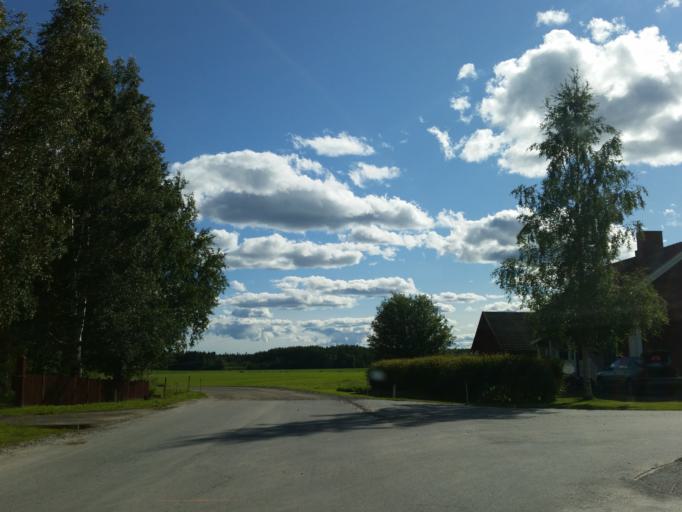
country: SE
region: Vaesterbotten
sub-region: Robertsfors Kommun
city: Robertsfors
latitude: 64.1863
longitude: 20.8438
